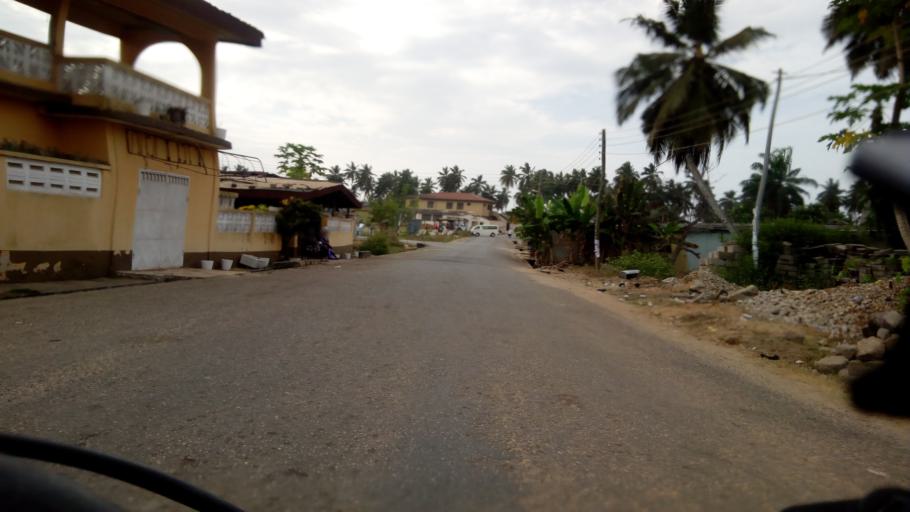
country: GH
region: Central
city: Cape Coast
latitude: 5.1027
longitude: -1.2791
